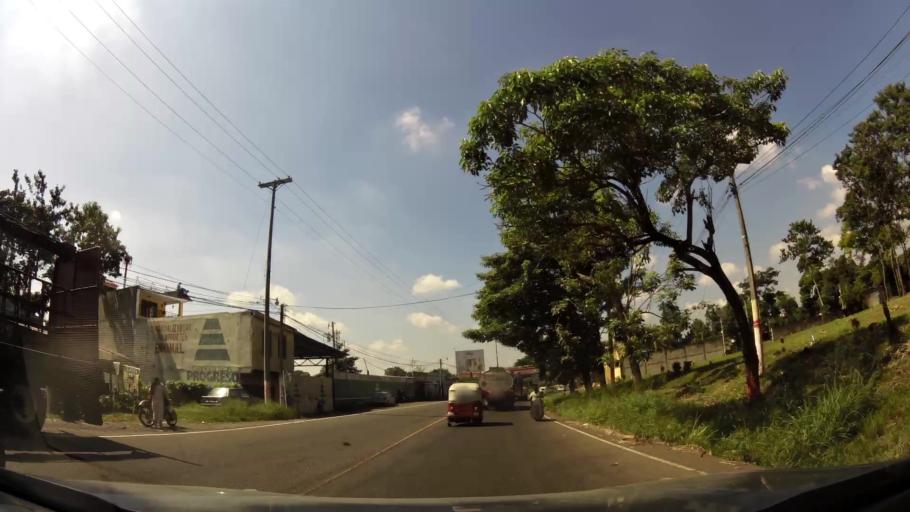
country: GT
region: Suchitepeque
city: Mazatenango
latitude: 14.5323
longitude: -91.4823
